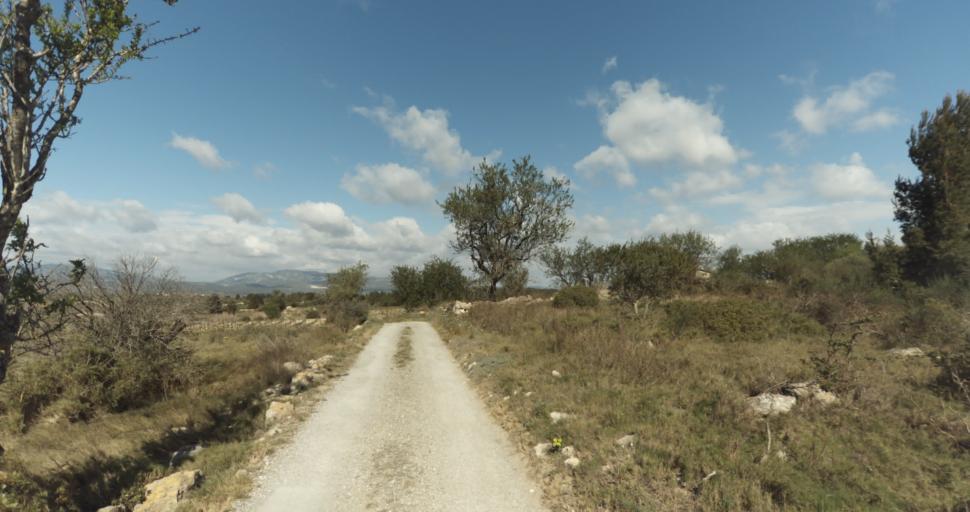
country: FR
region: Languedoc-Roussillon
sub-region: Departement de l'Aude
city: Leucate
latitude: 42.9286
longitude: 3.0273
